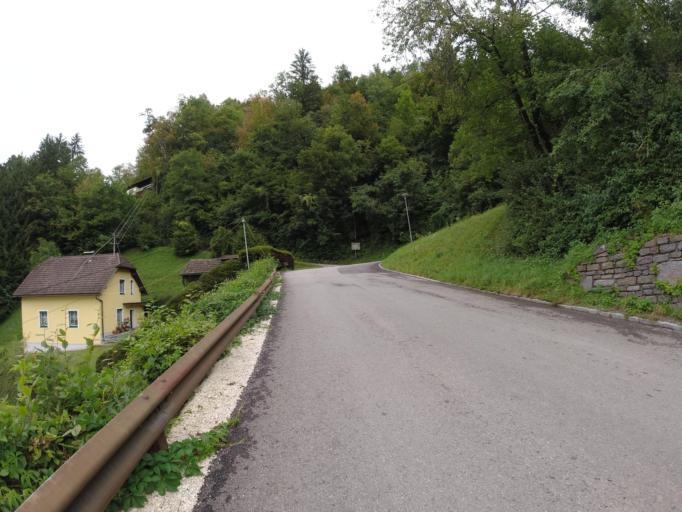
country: AT
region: Carinthia
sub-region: Politischer Bezirk Volkermarkt
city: Bad Eisenkappel
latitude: 46.4908
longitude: 14.5899
